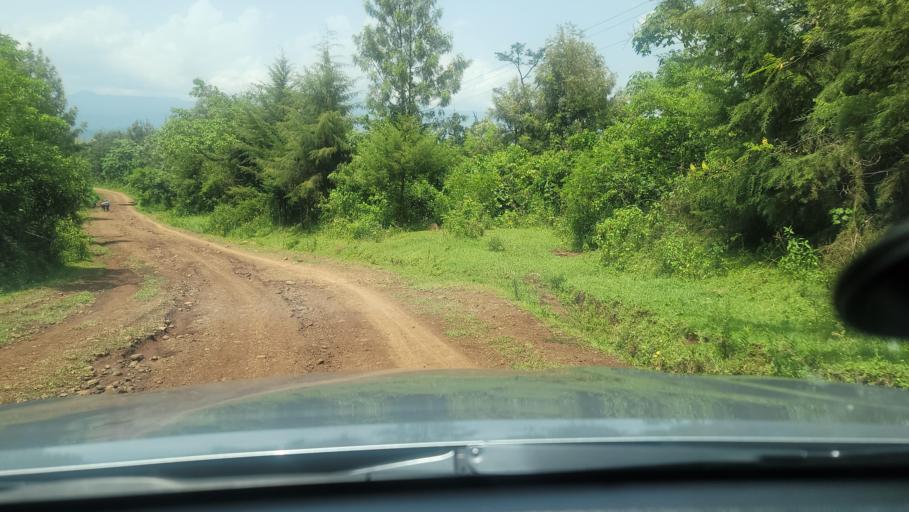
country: ET
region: Oromiya
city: Agaro
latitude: 7.8077
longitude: 36.4132
